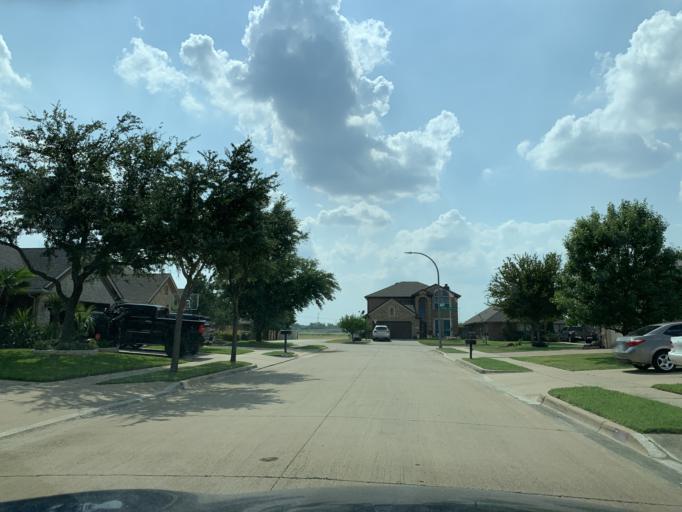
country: US
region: Texas
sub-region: Tarrant County
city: Richland Hills
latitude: 32.8033
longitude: -97.2008
